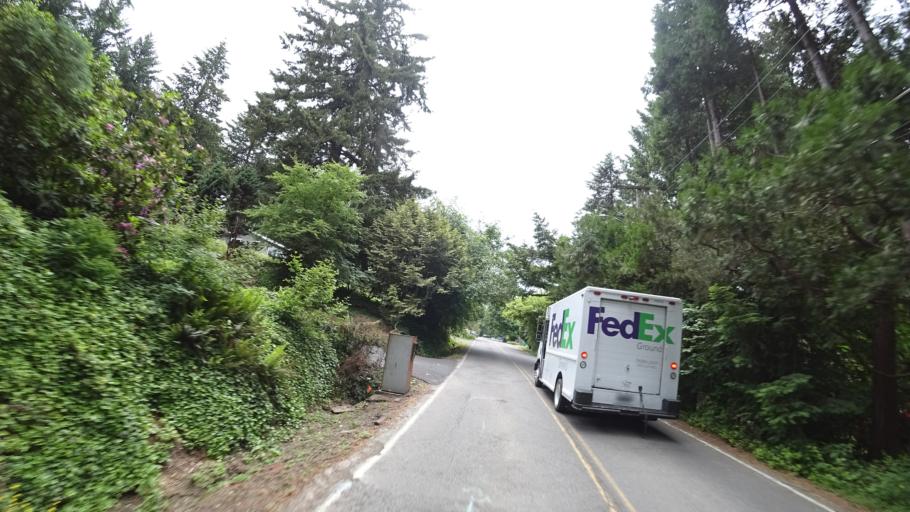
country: US
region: Oregon
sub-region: Clackamas County
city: Lake Oswego
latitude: 45.4514
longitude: -122.6958
